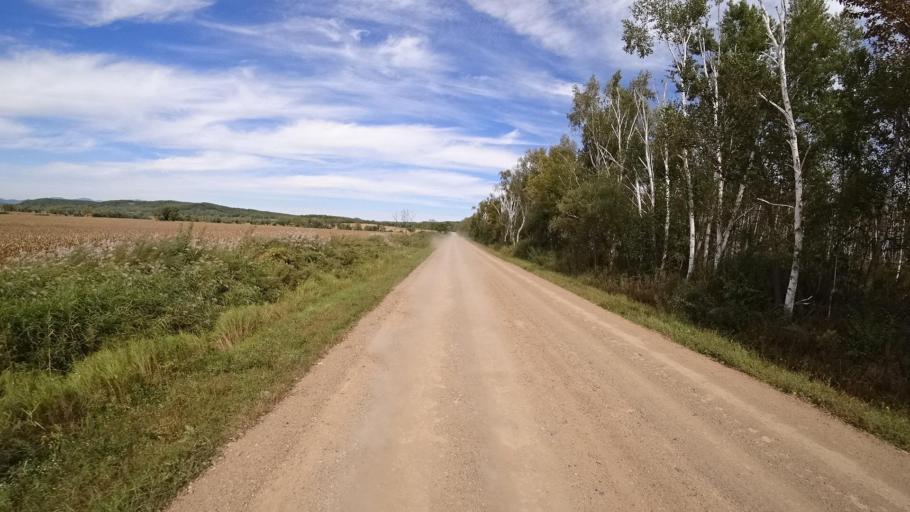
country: RU
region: Primorskiy
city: Yakovlevka
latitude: 44.5843
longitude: 133.6010
